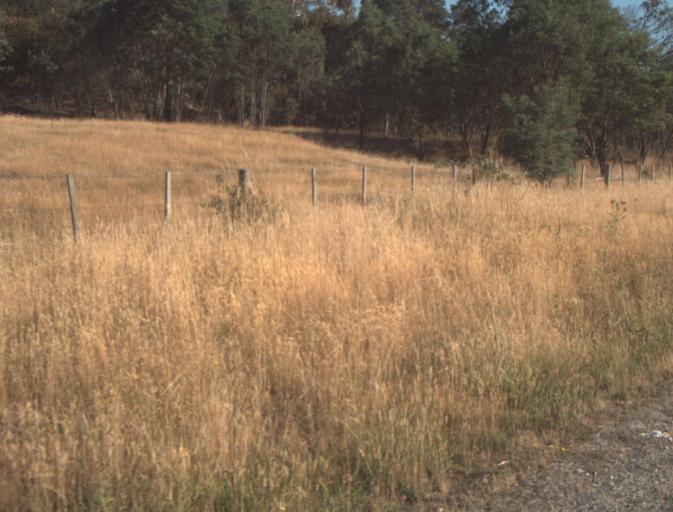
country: AU
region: Tasmania
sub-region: Launceston
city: Newstead
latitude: -41.4427
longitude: 147.2537
